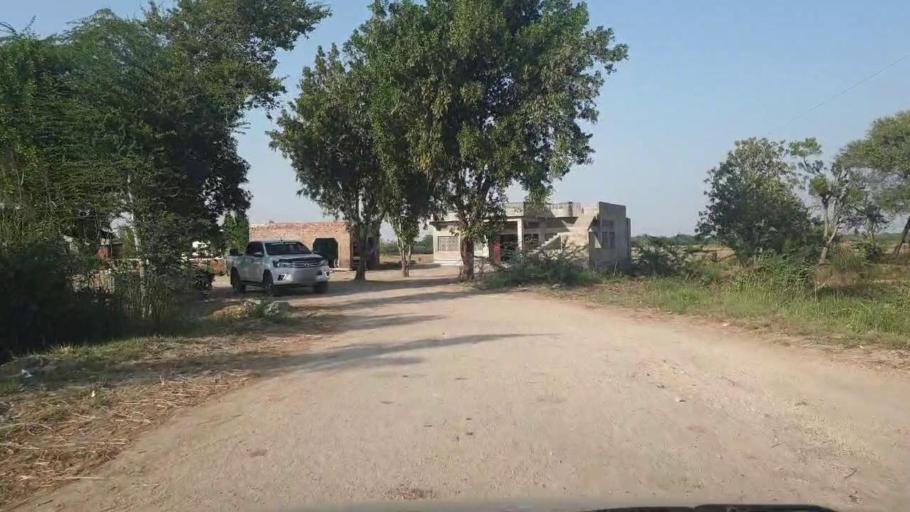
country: PK
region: Sindh
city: Badin
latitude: 24.6571
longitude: 68.8112
